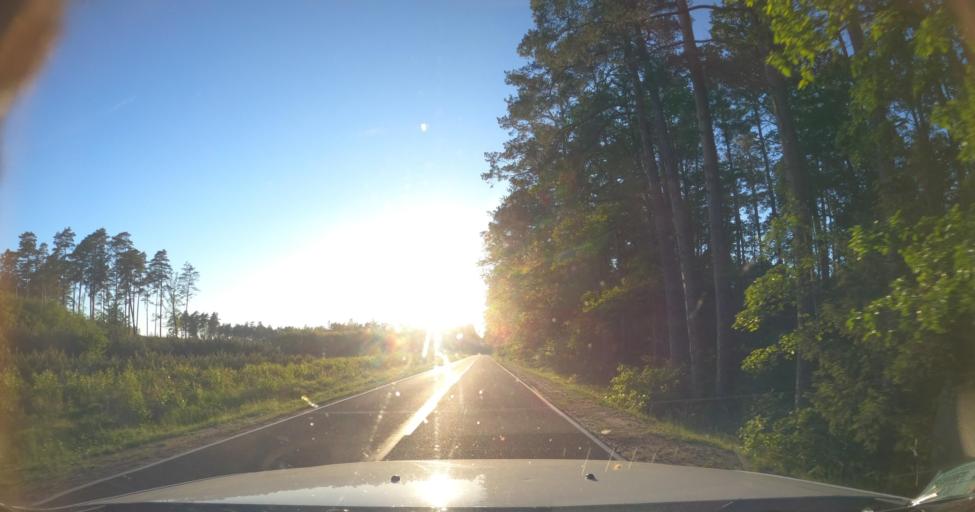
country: PL
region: Pomeranian Voivodeship
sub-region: Powiat slupski
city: Potegowo
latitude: 54.4015
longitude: 17.4586
